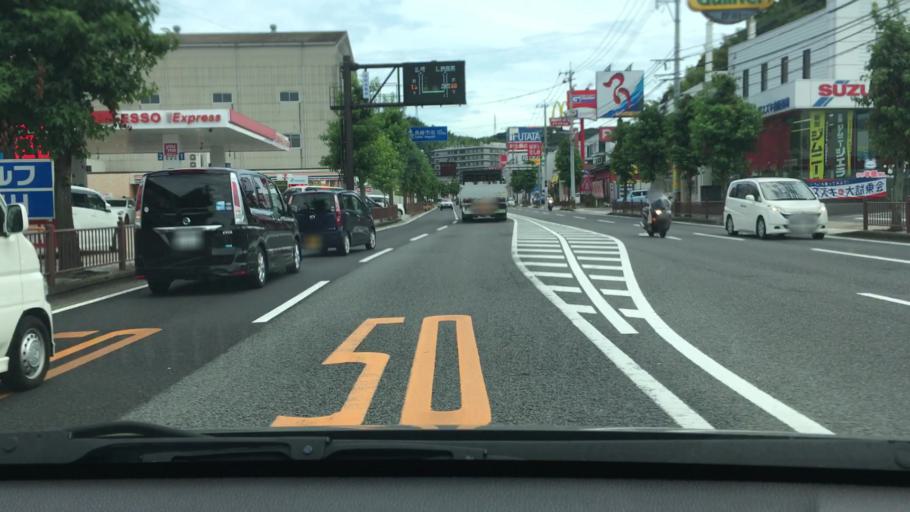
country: JP
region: Nagasaki
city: Togitsu
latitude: 32.8254
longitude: 129.8483
